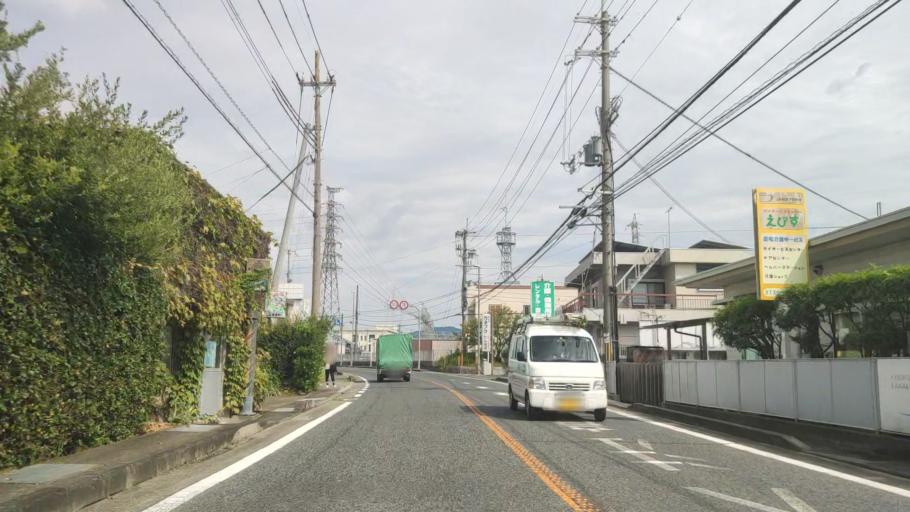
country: JP
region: Wakayama
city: Hashimoto
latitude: 34.3031
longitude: 135.5638
